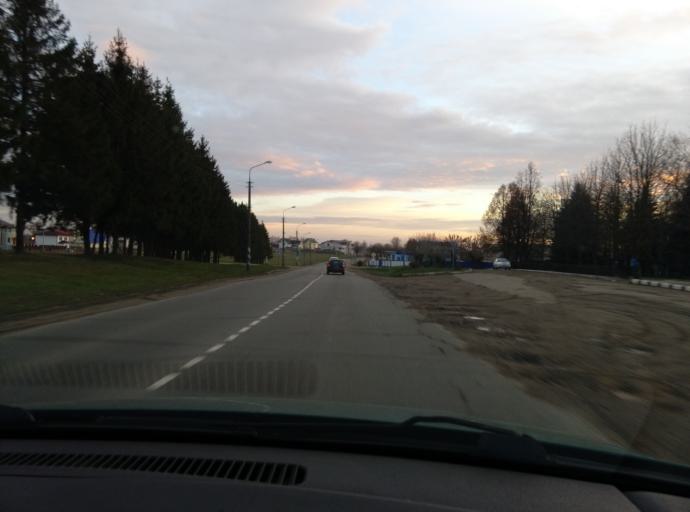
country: BY
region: Minsk
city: Horad Barysaw
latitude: 54.2665
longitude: 28.4996
